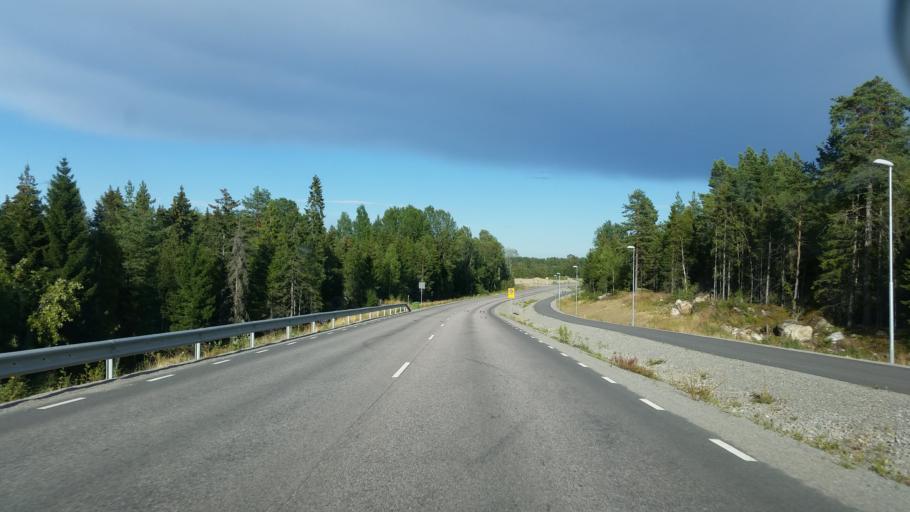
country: SE
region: Gaevleborg
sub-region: Hudiksvalls Kommun
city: Hudiksvall
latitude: 61.7504
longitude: 17.0991
